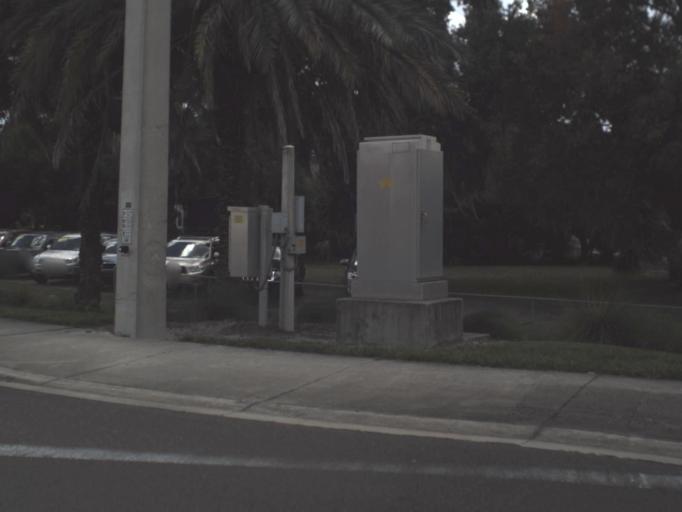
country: US
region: Florida
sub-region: Polk County
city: Lakeland
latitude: 28.0442
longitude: -81.9471
